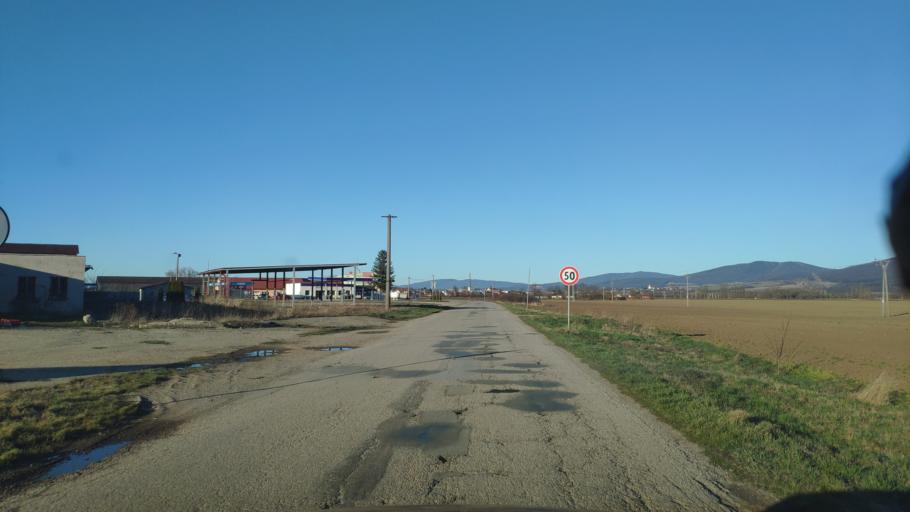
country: SK
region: Kosicky
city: Kosice
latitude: 48.5986
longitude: 21.3196
